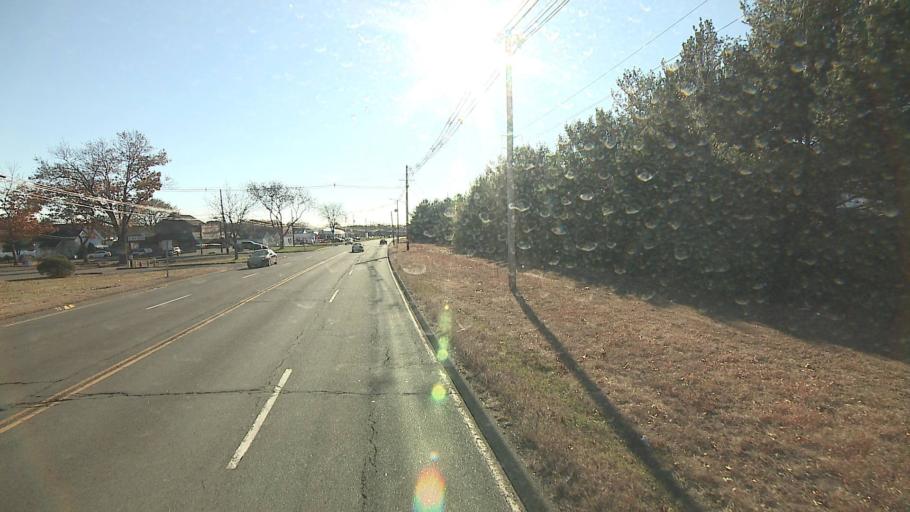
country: US
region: Connecticut
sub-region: New Haven County
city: Wallingford Center
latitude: 41.4340
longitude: -72.8346
